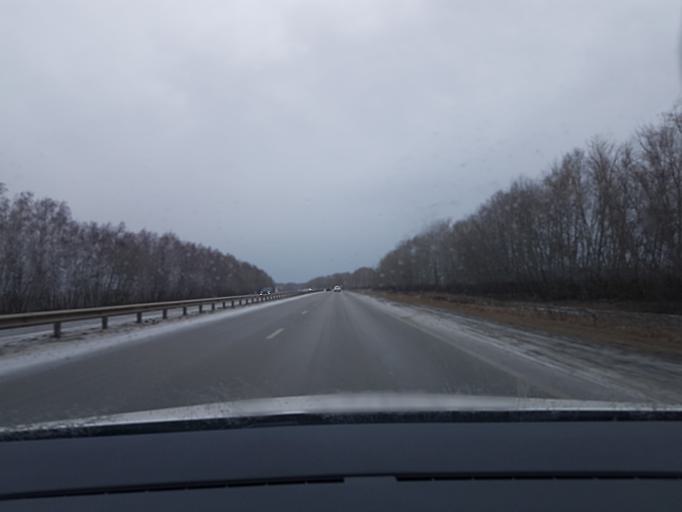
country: RU
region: Tambov
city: Selezni
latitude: 52.7653
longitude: 41.1071
